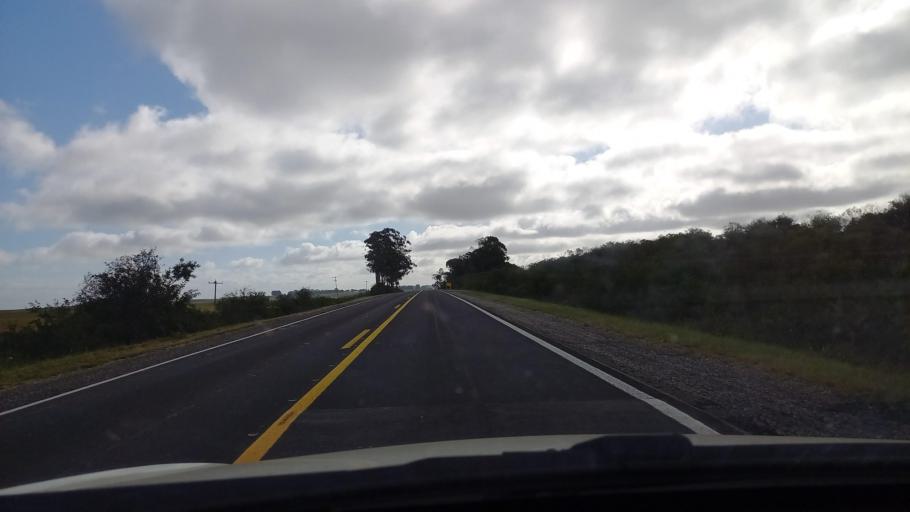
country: BR
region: Rio Grande do Sul
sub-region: Dom Pedrito
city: Dom Pedrito
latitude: -30.8933
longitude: -54.8543
